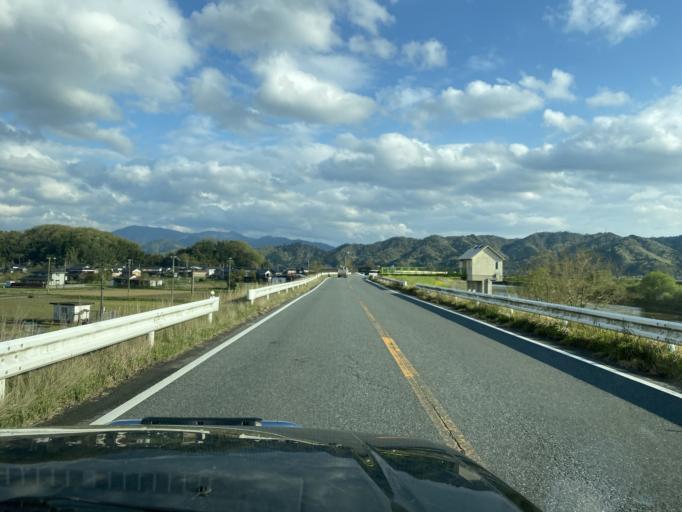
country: JP
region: Hyogo
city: Toyooka
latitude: 35.4982
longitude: 134.8400
